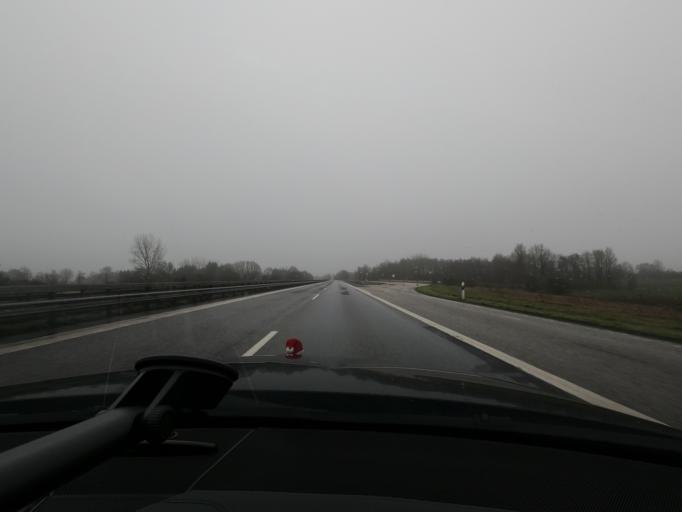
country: DE
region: Schleswig-Holstein
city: Lottorf
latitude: 54.4313
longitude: 9.5961
